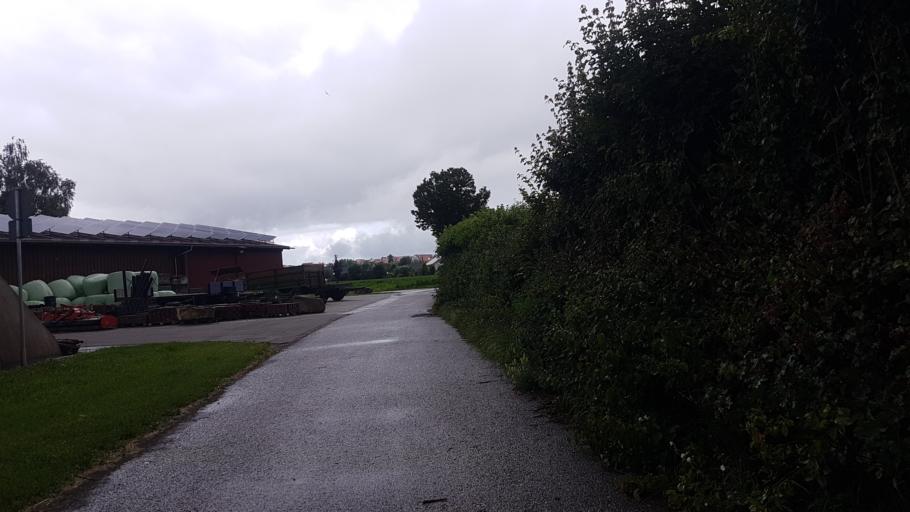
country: DE
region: Baden-Wuerttemberg
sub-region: Tuebingen Region
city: Rottenacker
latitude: 48.2287
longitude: 9.7009
